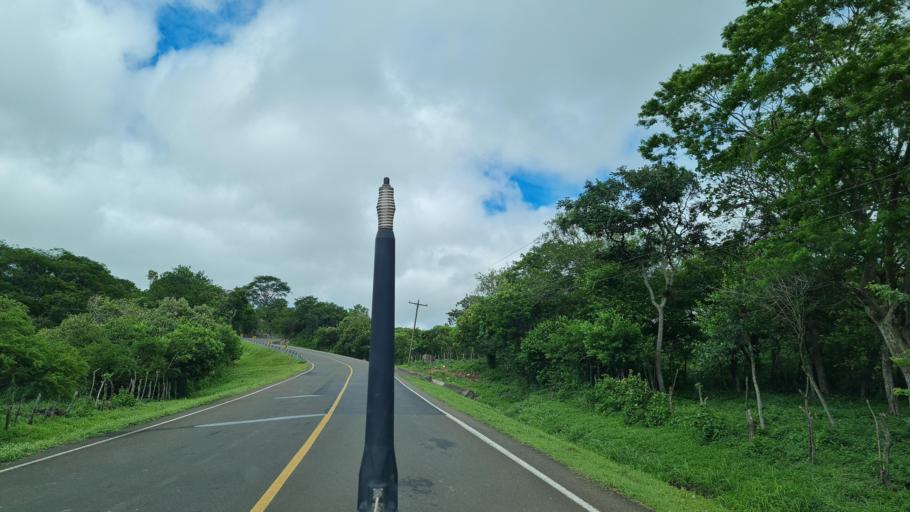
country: NI
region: Matagalpa
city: Terrabona
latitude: 12.5935
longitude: -85.9553
